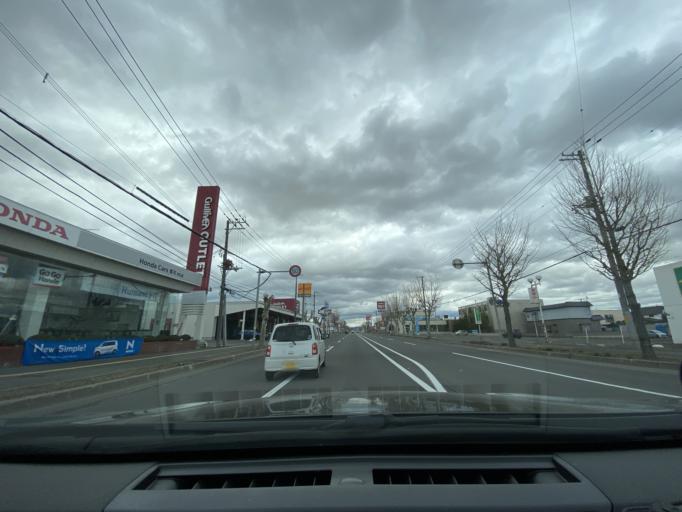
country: JP
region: Hokkaido
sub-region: Asahikawa-shi
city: Asahikawa
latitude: 43.8093
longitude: 142.3944
